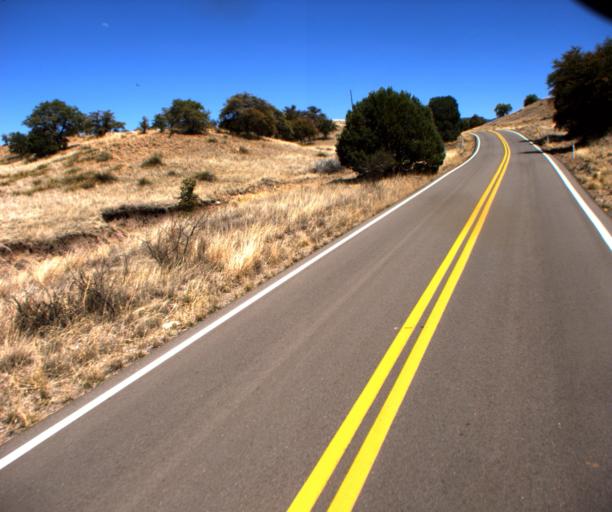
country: US
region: Arizona
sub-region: Cochise County
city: Huachuca City
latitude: 31.5437
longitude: -110.5233
